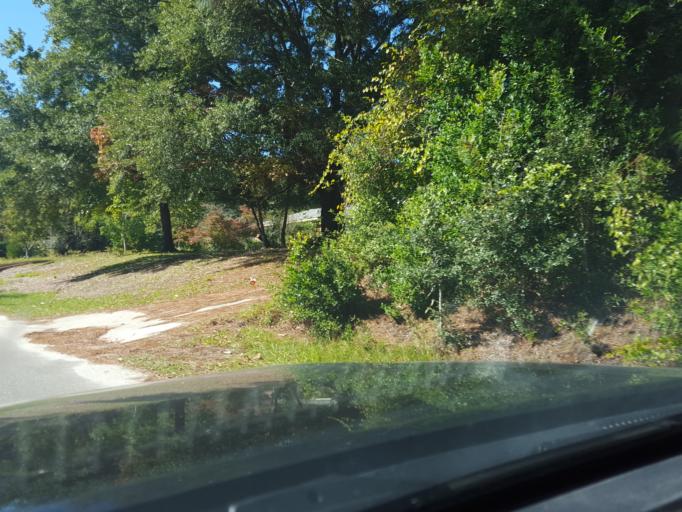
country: US
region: North Carolina
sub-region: New Hanover County
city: Seagate
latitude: 34.2006
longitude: -77.8813
